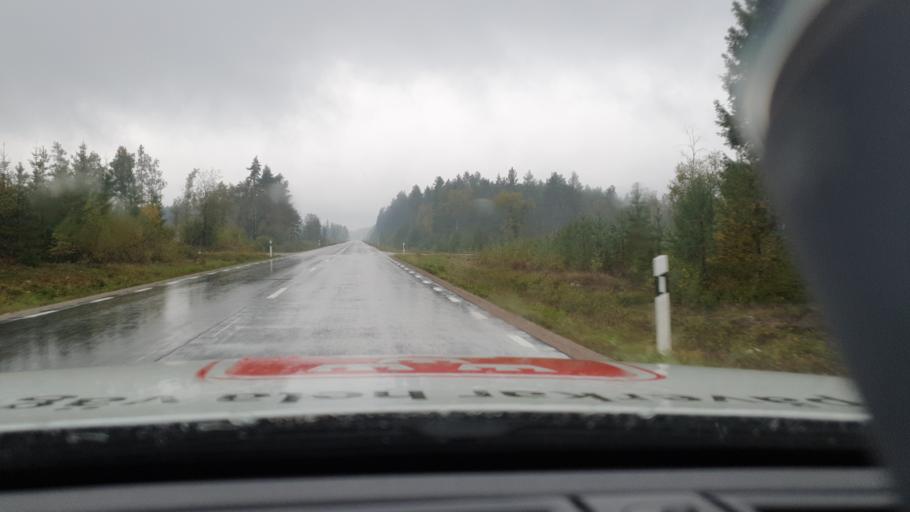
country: SE
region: Uppsala
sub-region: Tierps Kommun
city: Tierp
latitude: 60.3053
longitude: 17.5599
